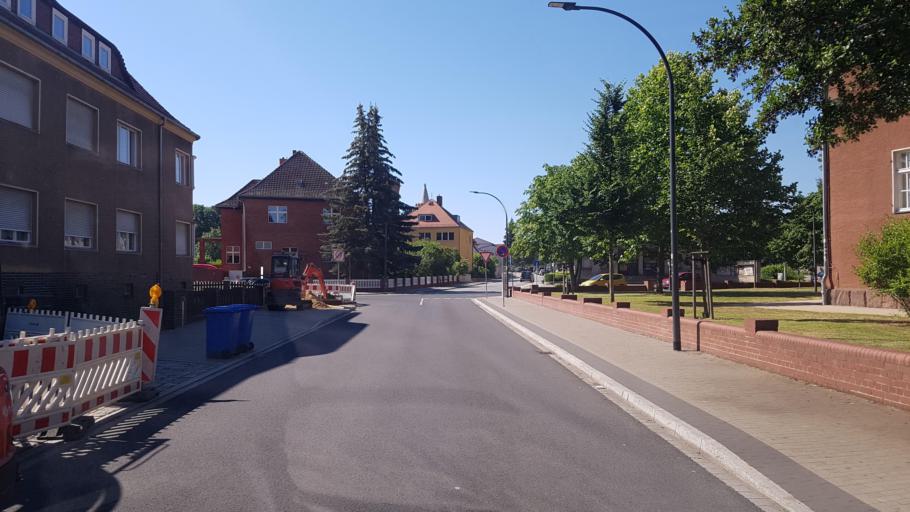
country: DE
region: Brandenburg
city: Juterbog
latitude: 51.9927
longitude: 13.0751
